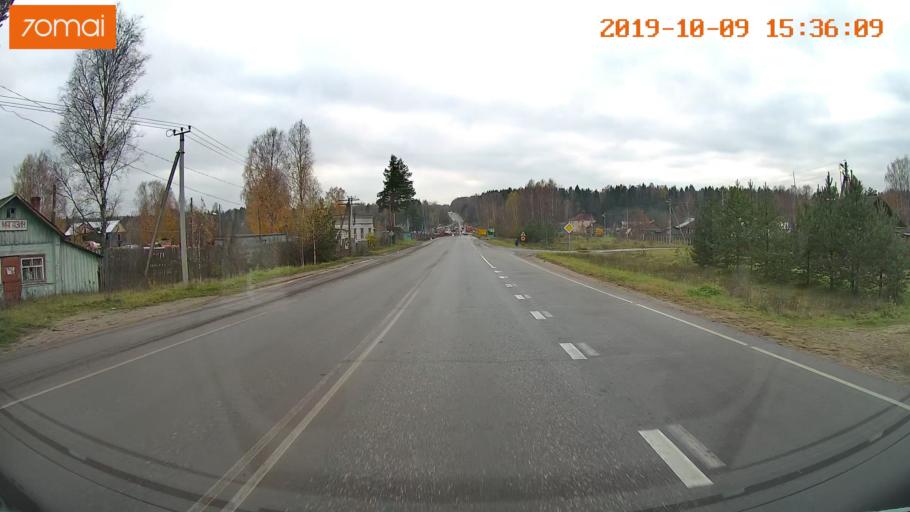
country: RU
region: Kostroma
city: Oktyabr'skiy
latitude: 57.9255
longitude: 41.2140
